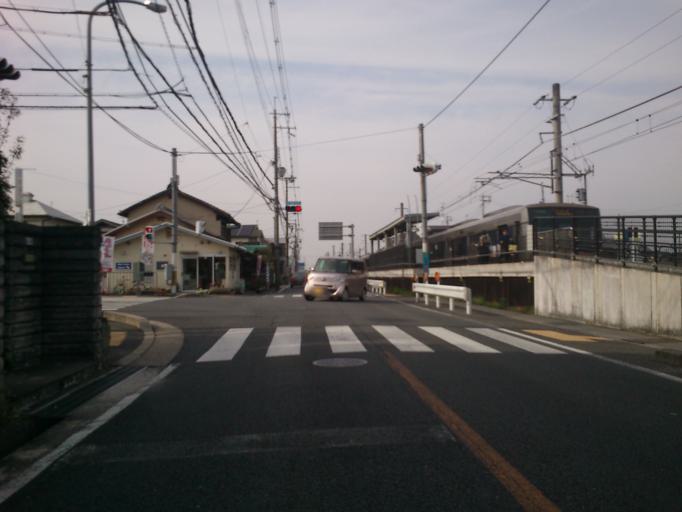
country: JP
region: Kyoto
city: Tanabe
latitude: 34.7793
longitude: 135.7886
